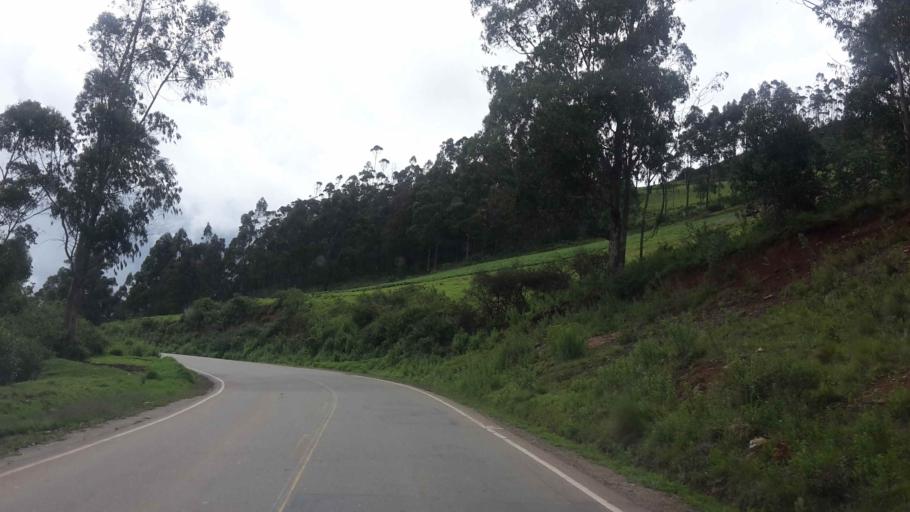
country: BO
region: Cochabamba
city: Totora
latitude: -17.5571
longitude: -65.3438
